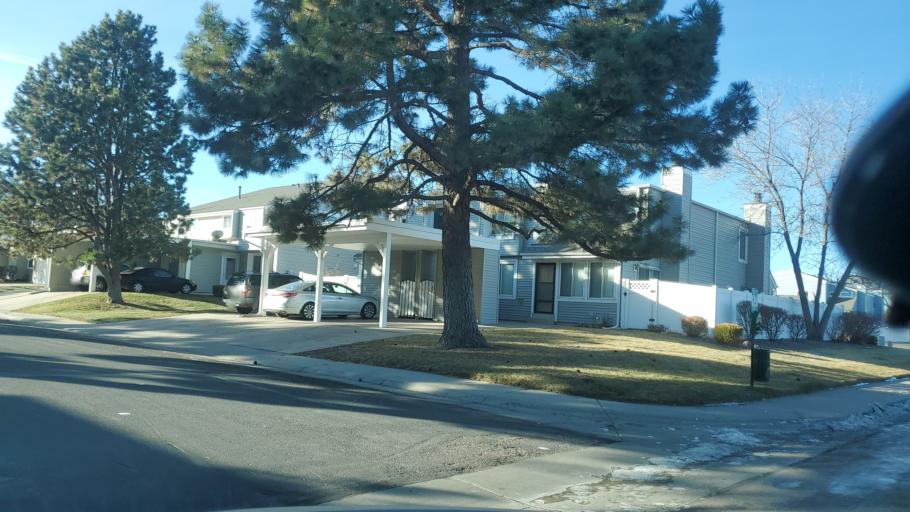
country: US
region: Colorado
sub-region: Adams County
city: Northglenn
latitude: 39.9116
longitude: -104.9435
